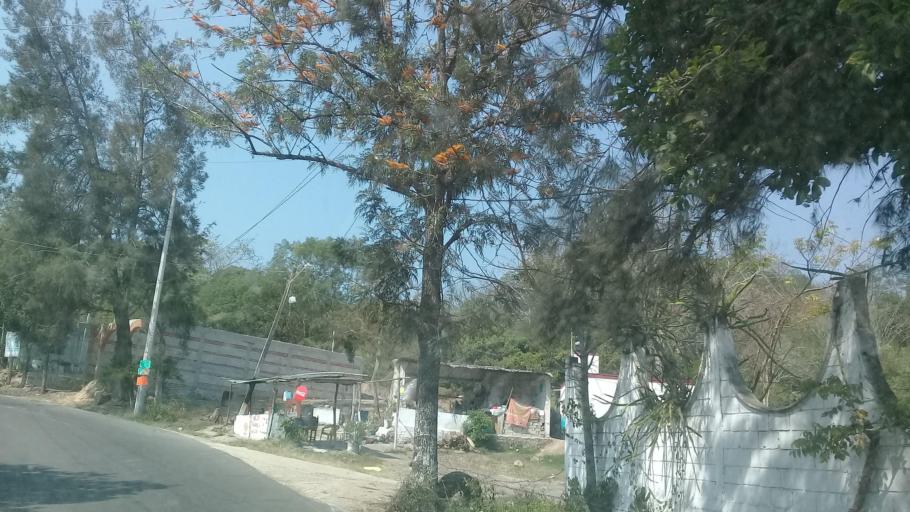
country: MX
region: Veracruz
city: El Castillo
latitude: 19.5712
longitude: -96.8355
